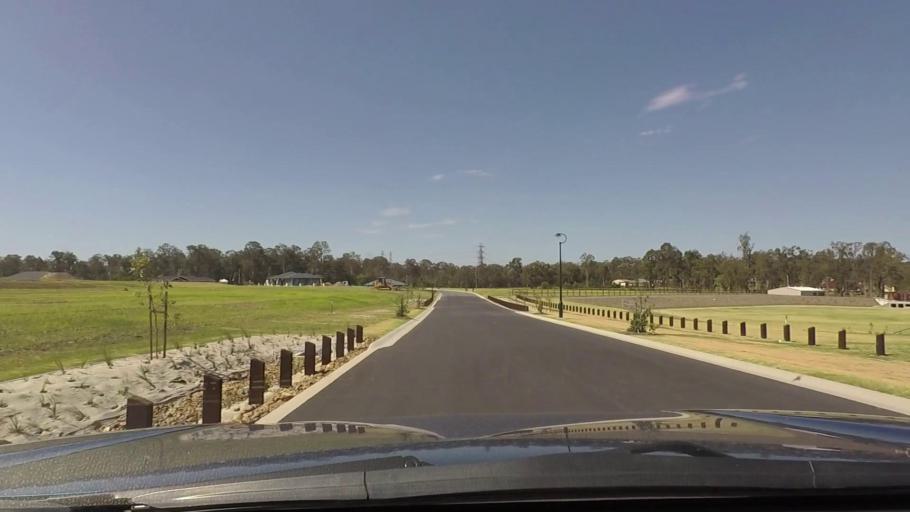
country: AU
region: Queensland
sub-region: Logan
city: North Maclean
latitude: -27.7373
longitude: 152.9513
